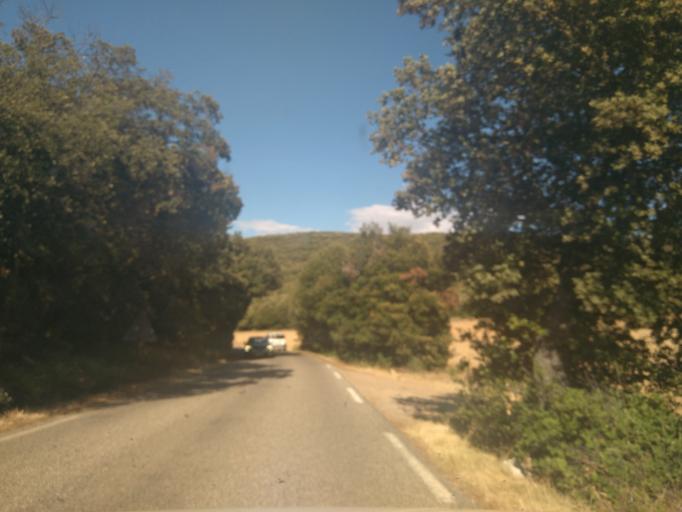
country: FR
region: Provence-Alpes-Cote d'Azur
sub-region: Departement du Var
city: Regusse
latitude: 43.7276
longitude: 6.1254
